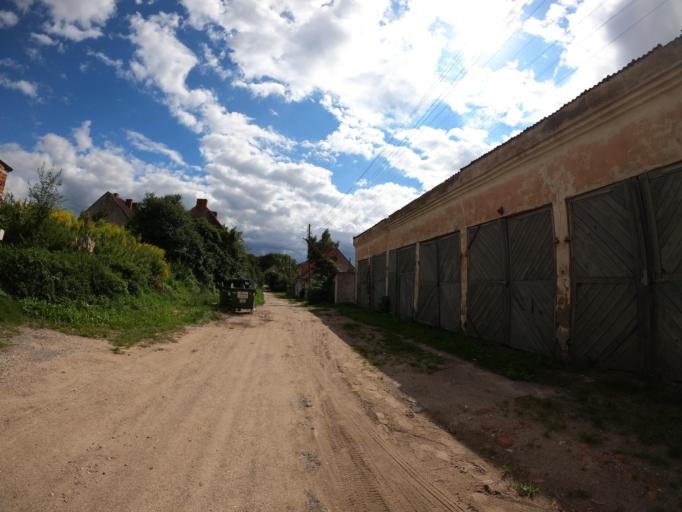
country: RU
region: Kaliningrad
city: Zheleznodorozhnyy
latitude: 54.3607
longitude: 21.3040
